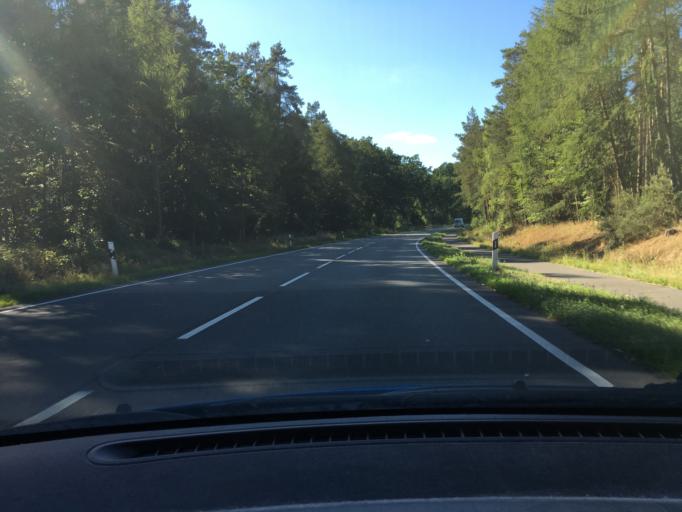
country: DE
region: Lower Saxony
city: Reinstorf
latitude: 53.2026
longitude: 10.6094
